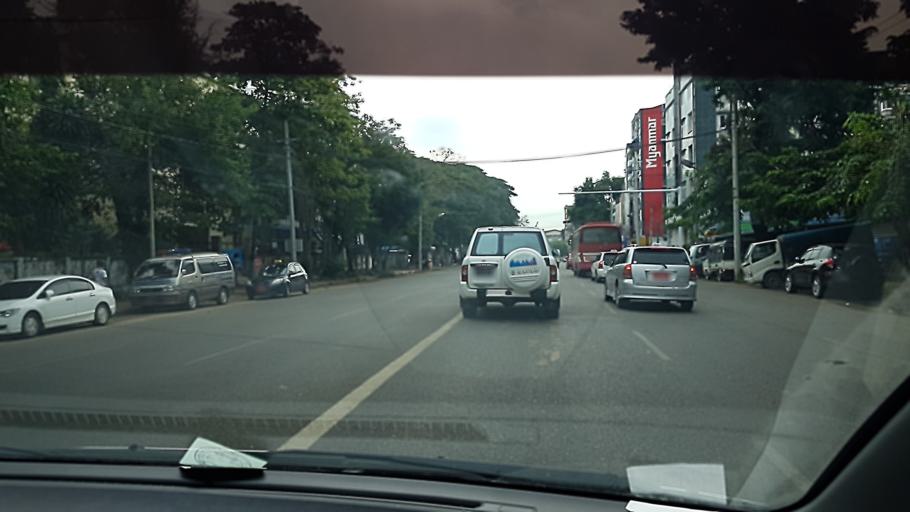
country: MM
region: Yangon
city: Yangon
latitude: 16.7903
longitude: 96.1281
